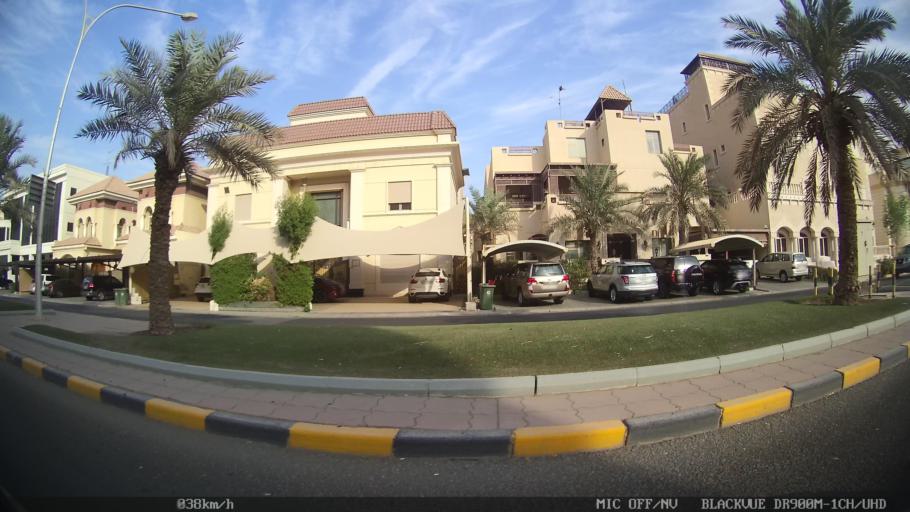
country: KW
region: Al Farwaniyah
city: Al Farwaniyah
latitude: 29.3067
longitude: 47.9717
